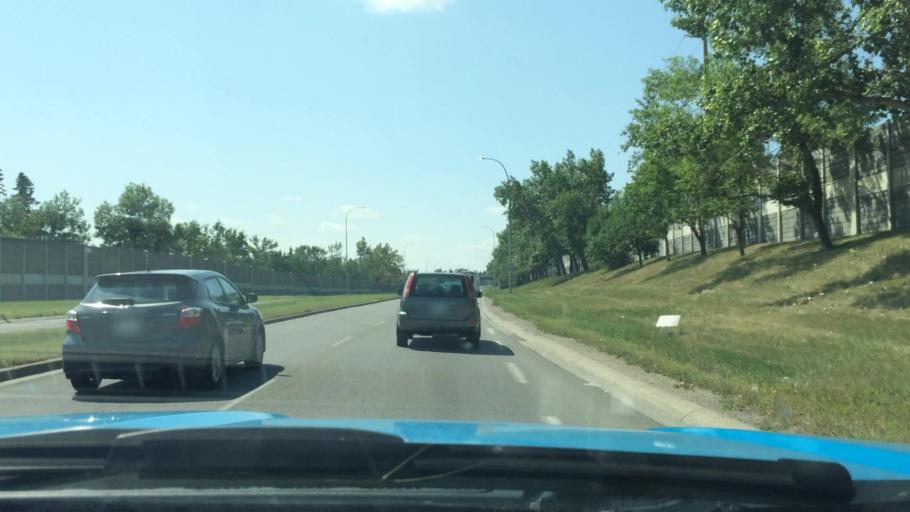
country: CA
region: Alberta
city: Calgary
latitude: 51.0956
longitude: -114.0845
